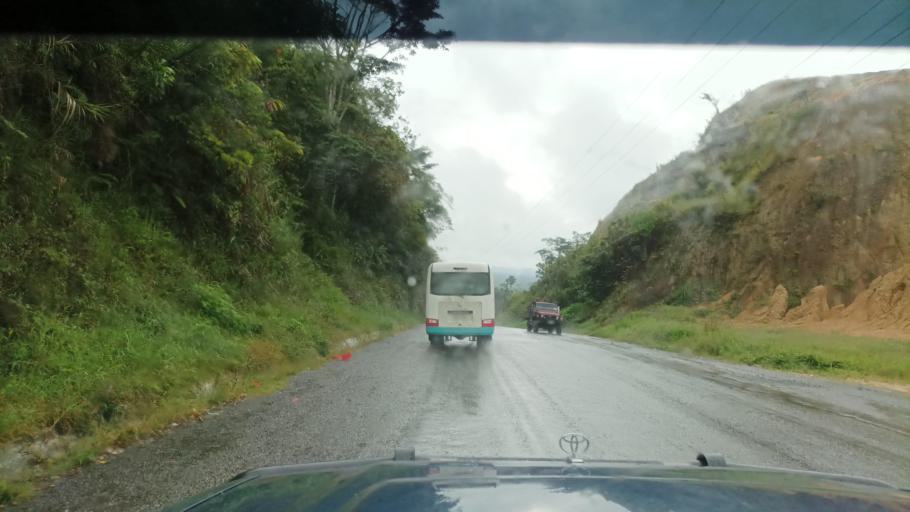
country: PG
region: Western Highlands
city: Rauna
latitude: -5.8275
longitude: 144.3725
